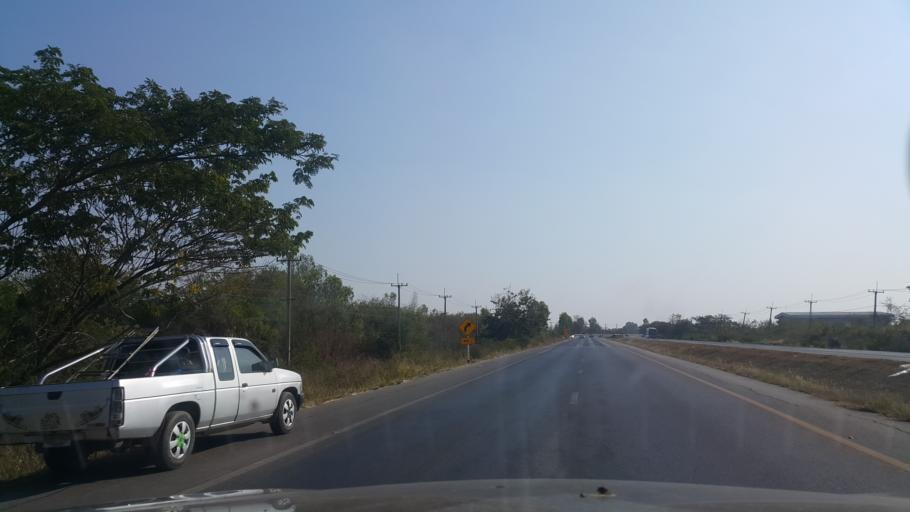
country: TH
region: Khon Kaen
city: Khon Kaen
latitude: 16.4253
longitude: 102.9173
